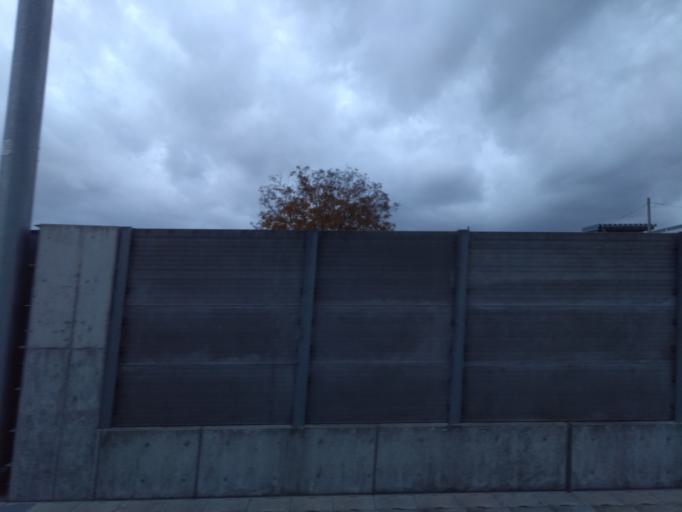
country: JP
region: Hokkaido
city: Nanae
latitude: 41.9040
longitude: 140.6512
